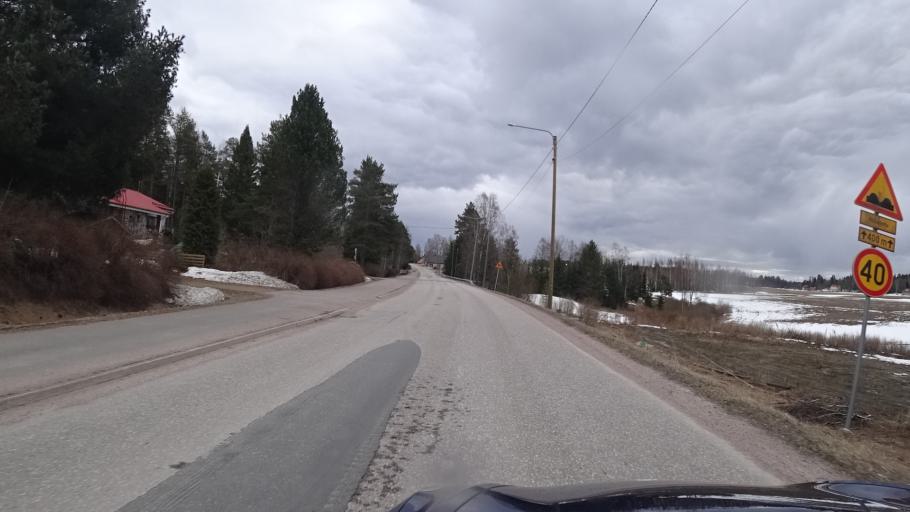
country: FI
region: Paijanne Tavastia
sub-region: Lahti
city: Nastola
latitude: 60.8765
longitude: 25.9995
